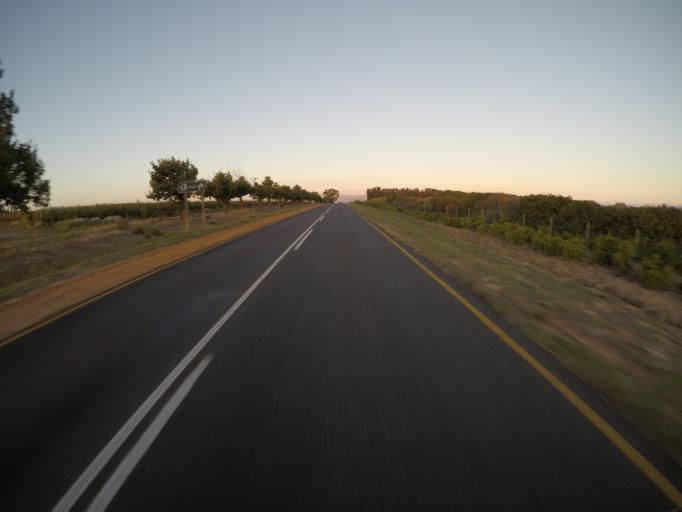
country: ZA
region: Western Cape
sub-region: Cape Winelands District Municipality
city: Paarl
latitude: -33.8048
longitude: 18.8841
